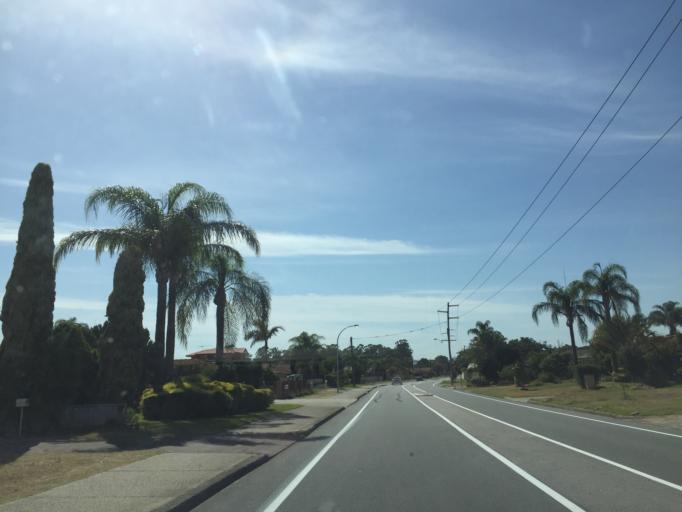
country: AU
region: Western Australia
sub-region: Gosnells
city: Thornlie
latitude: -32.0728
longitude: 115.9579
